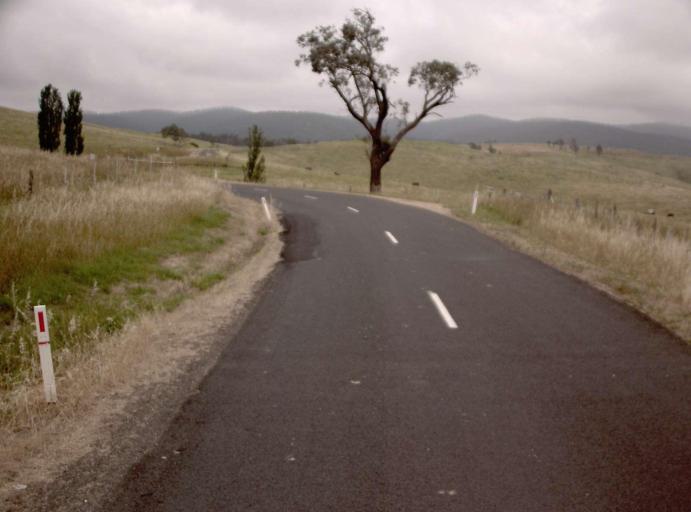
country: AU
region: Victoria
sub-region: Wellington
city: Heyfield
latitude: -37.8447
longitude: 146.7045
